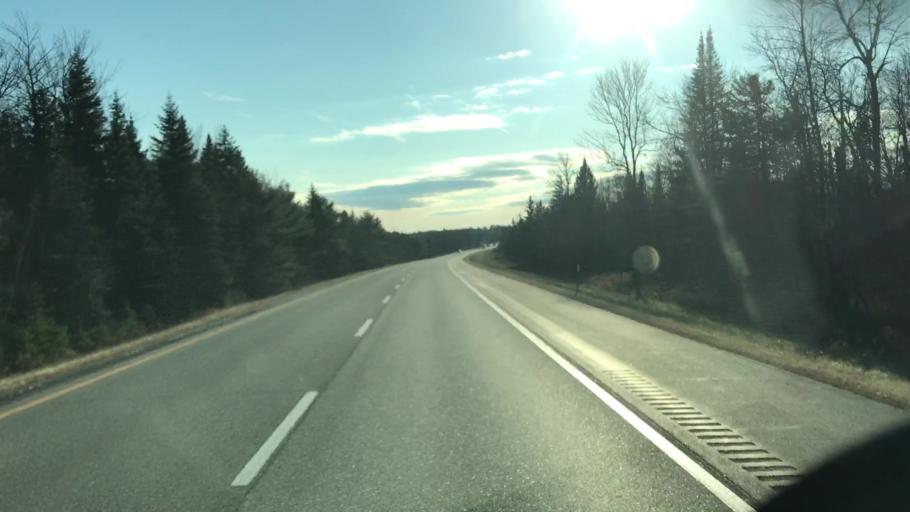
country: US
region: Maine
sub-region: Waldo County
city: Burnham
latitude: 44.7121
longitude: -69.4496
